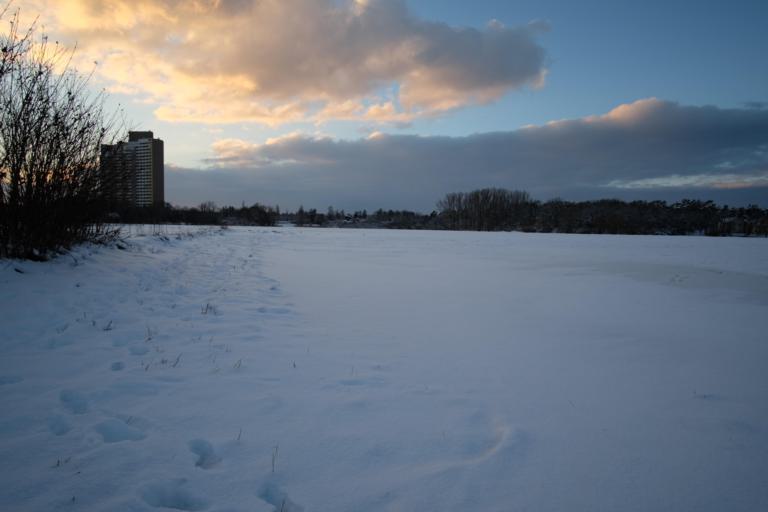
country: DE
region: Bavaria
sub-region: Regierungsbezirk Mittelfranken
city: Erlangen
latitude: 49.6082
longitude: 10.9875
